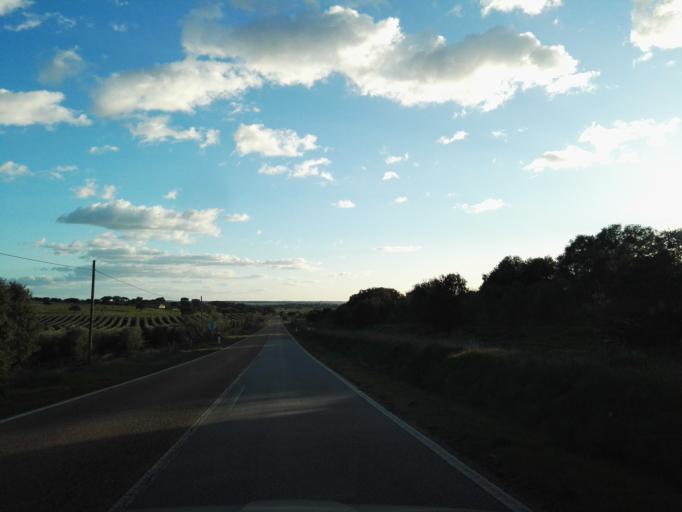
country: PT
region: Portalegre
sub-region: Elvas
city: Elvas
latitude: 38.8135
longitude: -7.1673
